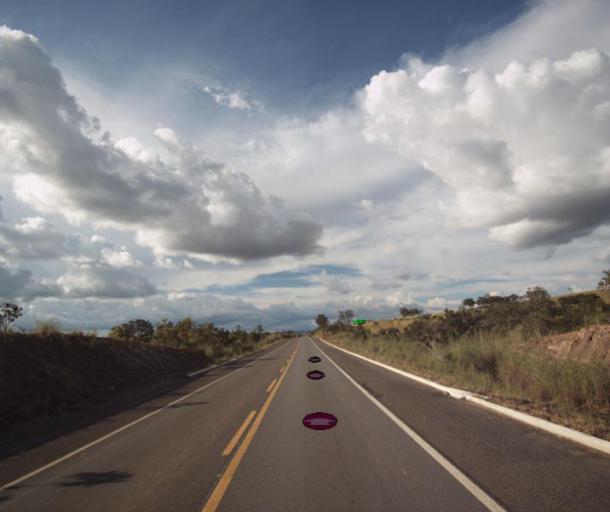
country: BR
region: Goias
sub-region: Barro Alto
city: Barro Alto
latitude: -14.8012
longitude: -48.6338
